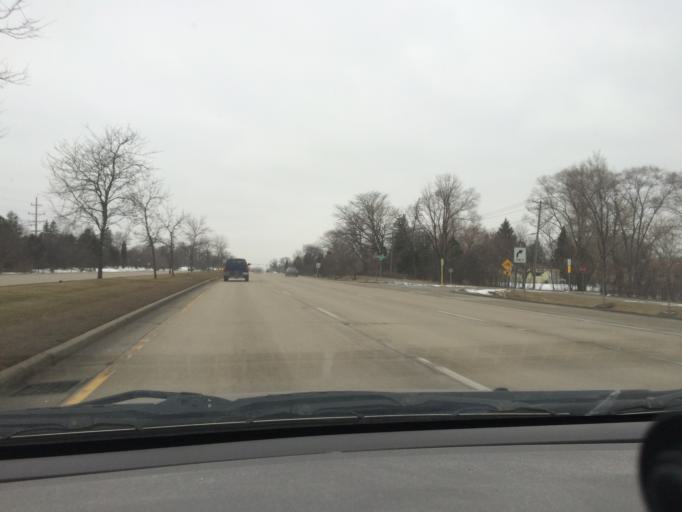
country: US
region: Illinois
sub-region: Cook County
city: Hoffman Estates
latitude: 42.0418
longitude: -88.0658
